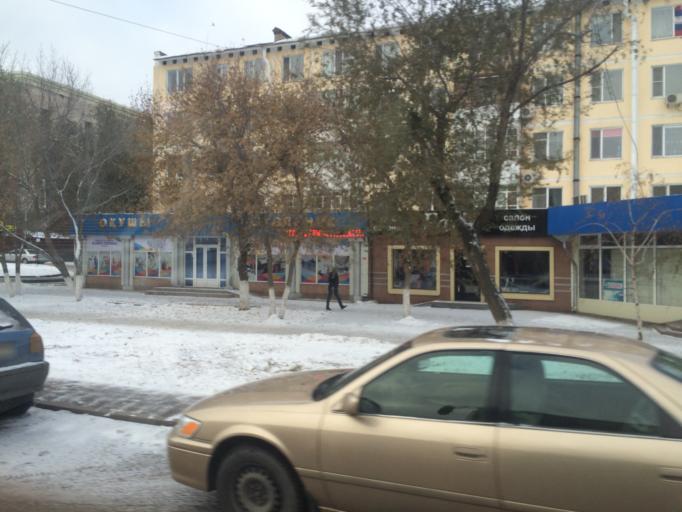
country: KZ
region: Astana Qalasy
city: Astana
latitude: 51.1733
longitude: 71.4193
